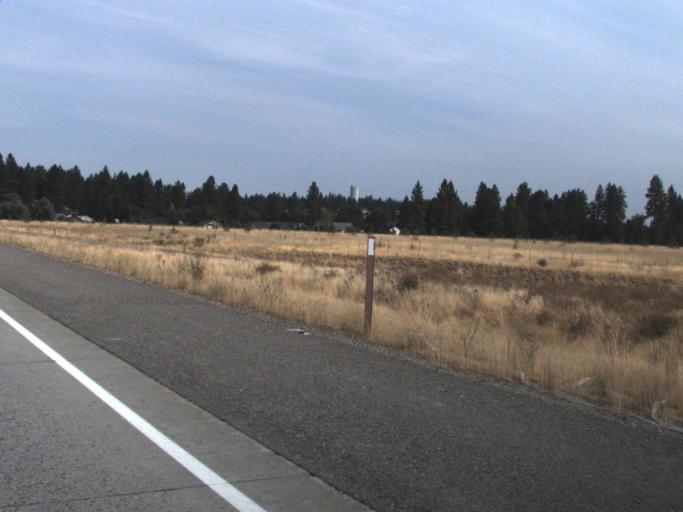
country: US
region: Washington
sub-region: Spokane County
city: Fairwood
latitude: 47.8062
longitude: -117.4055
